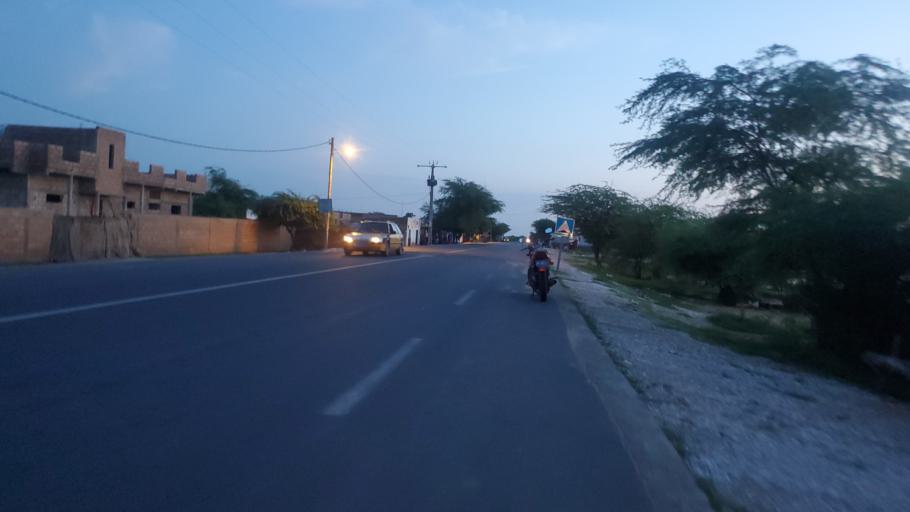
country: SN
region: Saint-Louis
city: Saint-Louis
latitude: 16.0691
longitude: -16.3911
